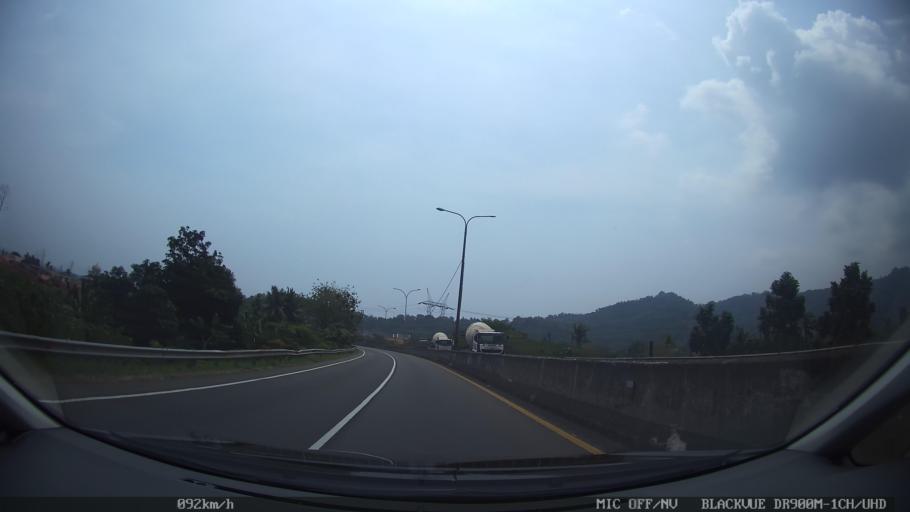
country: ID
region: Banten
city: Curug
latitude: -5.9841
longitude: 106.0311
